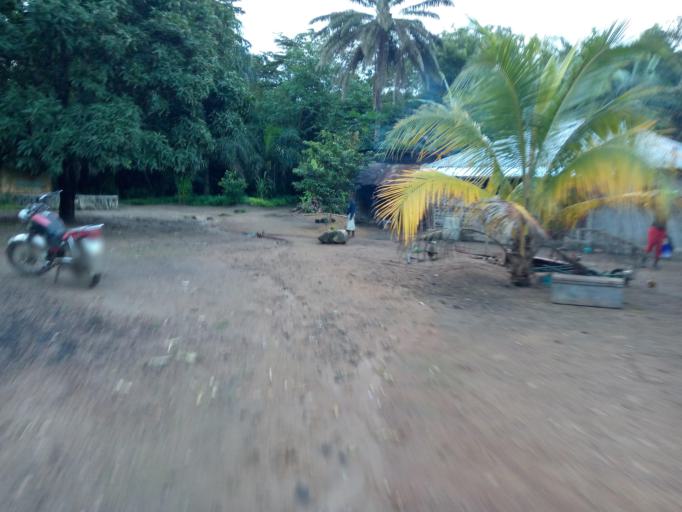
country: SL
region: Eastern Province
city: Buedu
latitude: 8.4892
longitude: -10.3433
